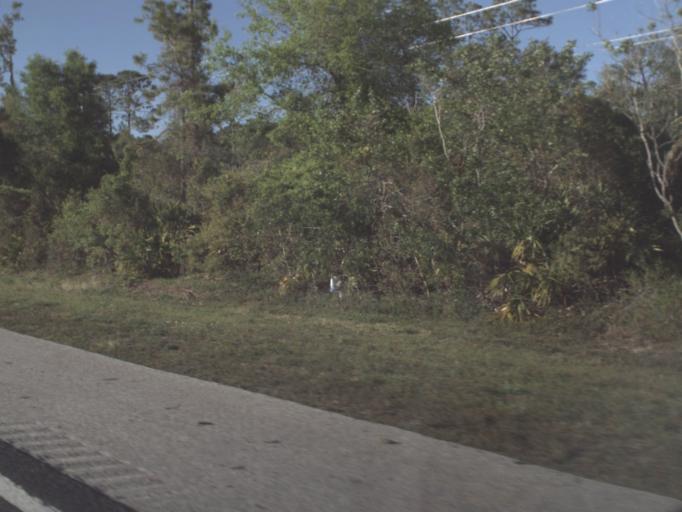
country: US
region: Florida
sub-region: Flagler County
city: Palm Coast
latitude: 29.5436
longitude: -81.2118
